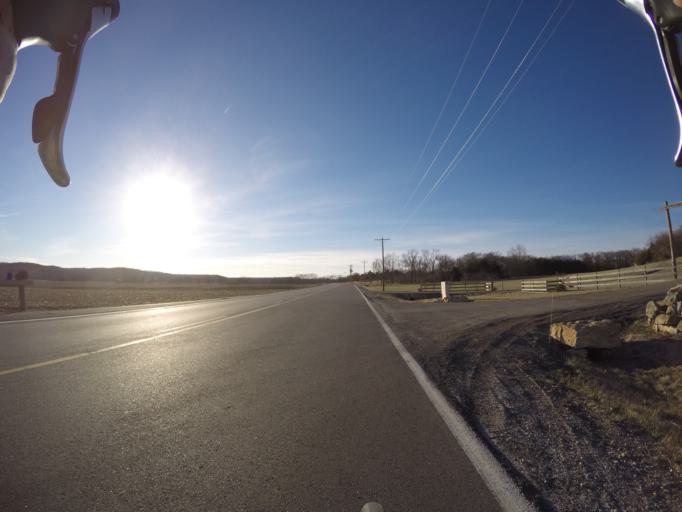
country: US
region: Kansas
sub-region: Riley County
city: Ogden
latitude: 39.2176
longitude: -96.6946
